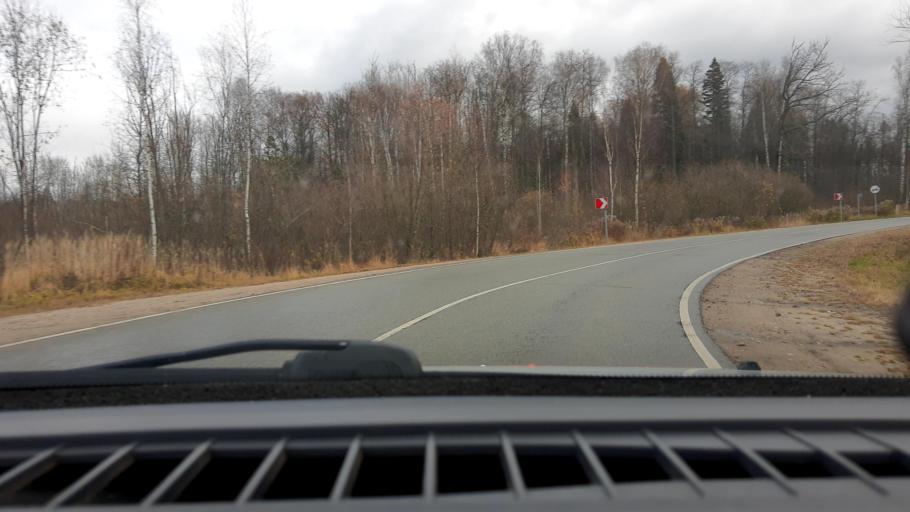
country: RU
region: Nizjnij Novgorod
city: Afonino
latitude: 56.1913
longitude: 44.0269
